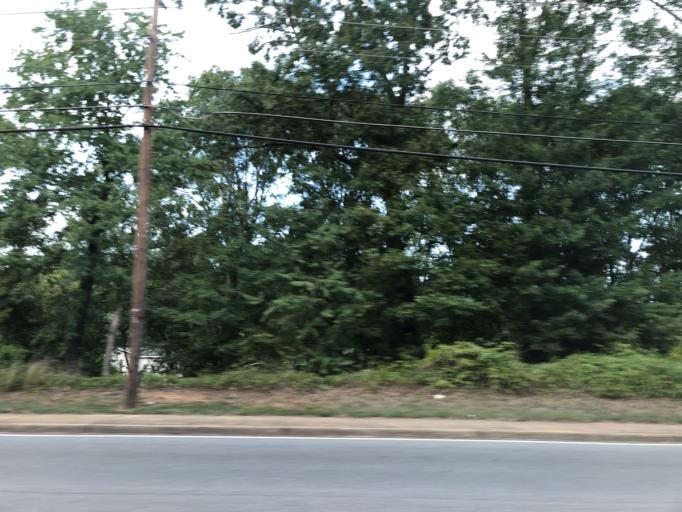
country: US
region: Georgia
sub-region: Clarke County
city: Athens
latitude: 33.9497
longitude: -83.3604
